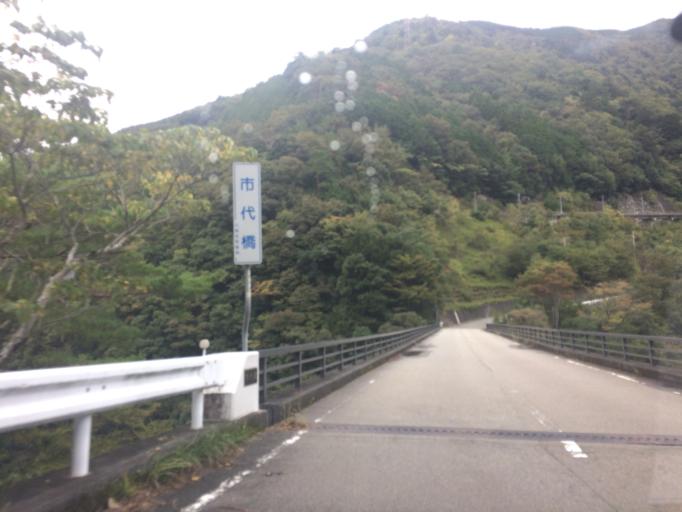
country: JP
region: Shizuoka
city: Shizuoka-shi
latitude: 35.1664
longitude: 138.1509
